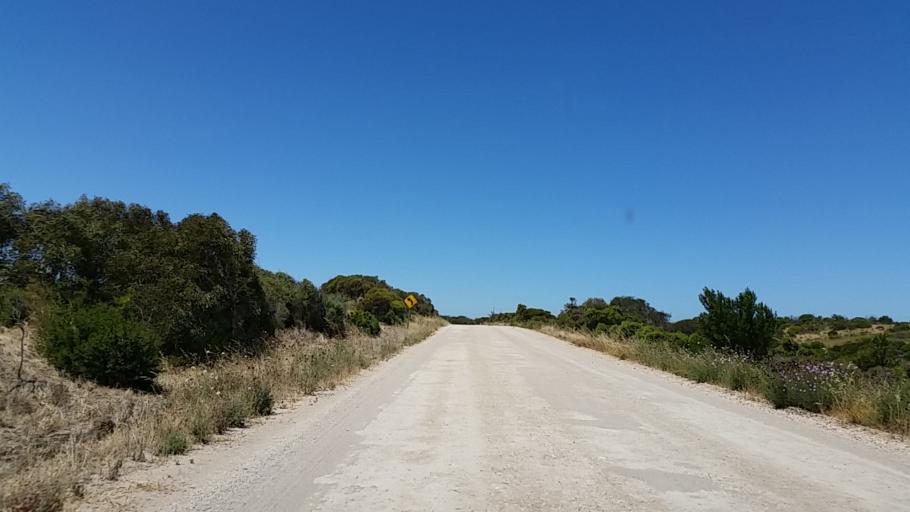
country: AU
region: South Australia
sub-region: Yorke Peninsula
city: Honiton
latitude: -35.1174
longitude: 137.3681
